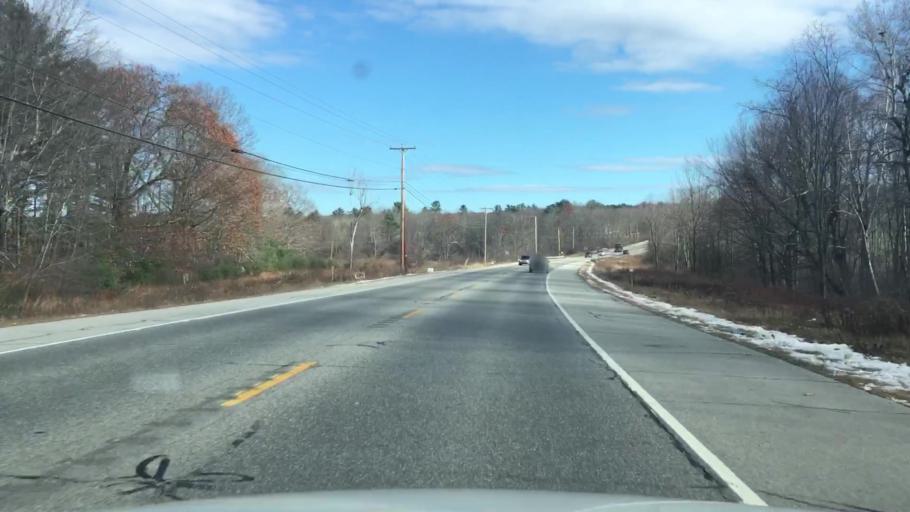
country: US
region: Maine
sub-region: Kennebec County
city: Winthrop
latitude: 44.3186
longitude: -69.9346
